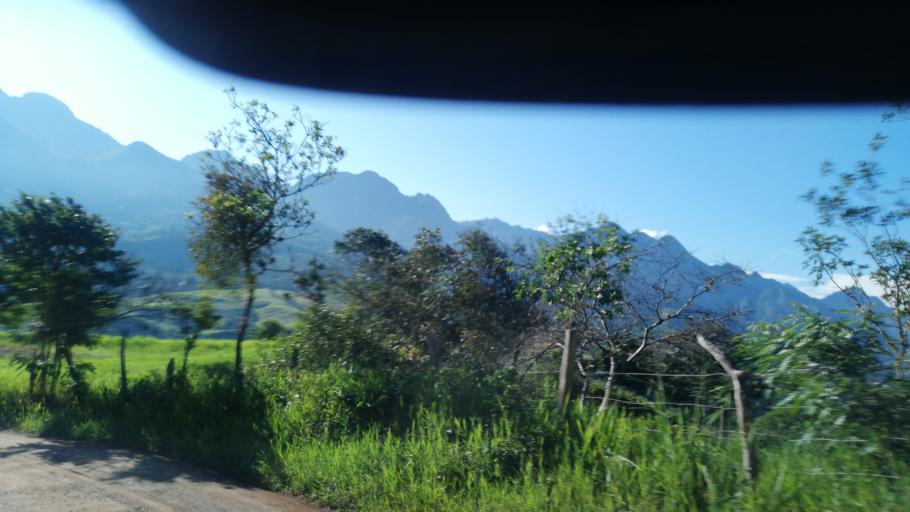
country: CO
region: Cundinamarca
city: Viani
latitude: 4.8352
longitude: -74.6224
